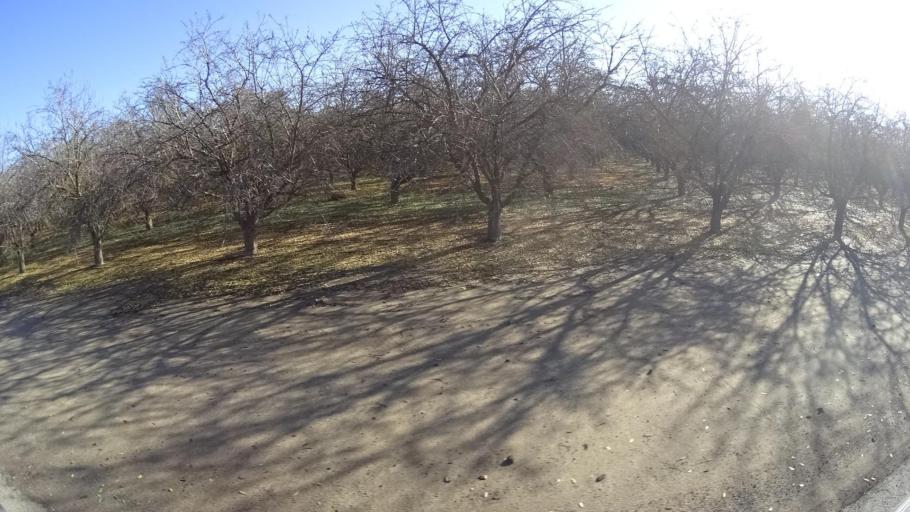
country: US
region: California
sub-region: Kern County
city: McFarland
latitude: 35.6984
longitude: -119.3119
